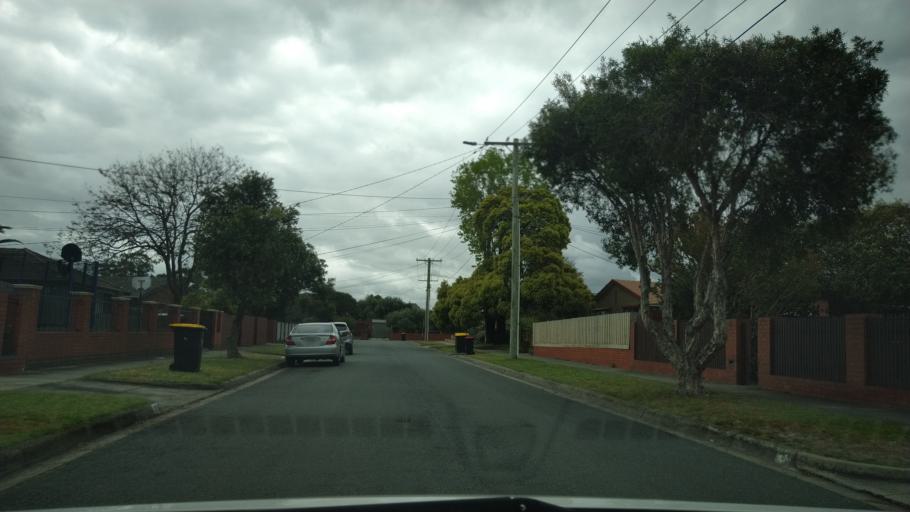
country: AU
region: Victoria
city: Heatherton
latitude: -37.9651
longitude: 145.0796
